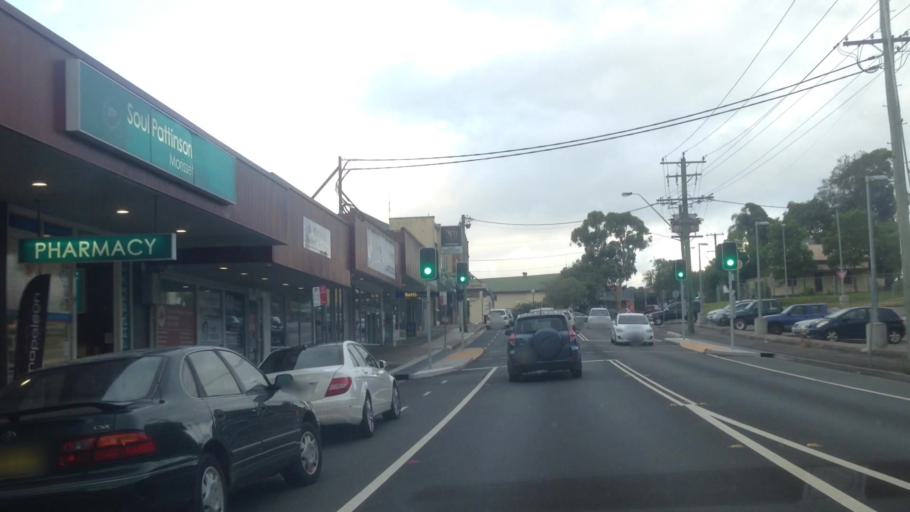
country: AU
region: New South Wales
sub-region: Lake Macquarie Shire
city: Dora Creek
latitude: -33.1090
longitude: 151.4868
